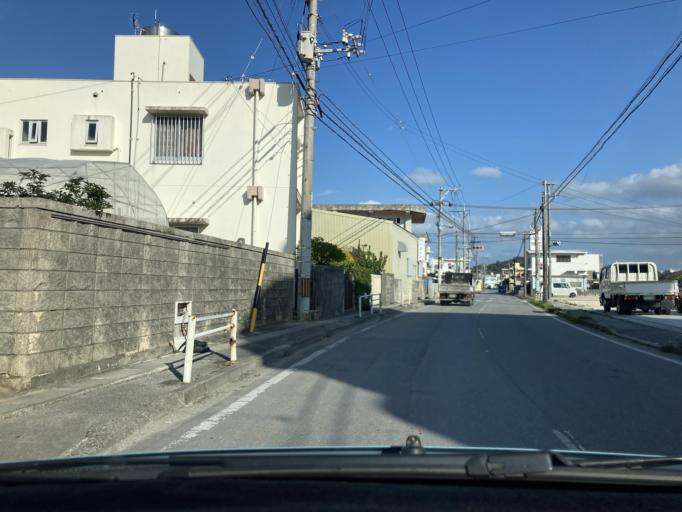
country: JP
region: Okinawa
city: Tomigusuku
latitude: 26.1648
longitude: 127.6649
